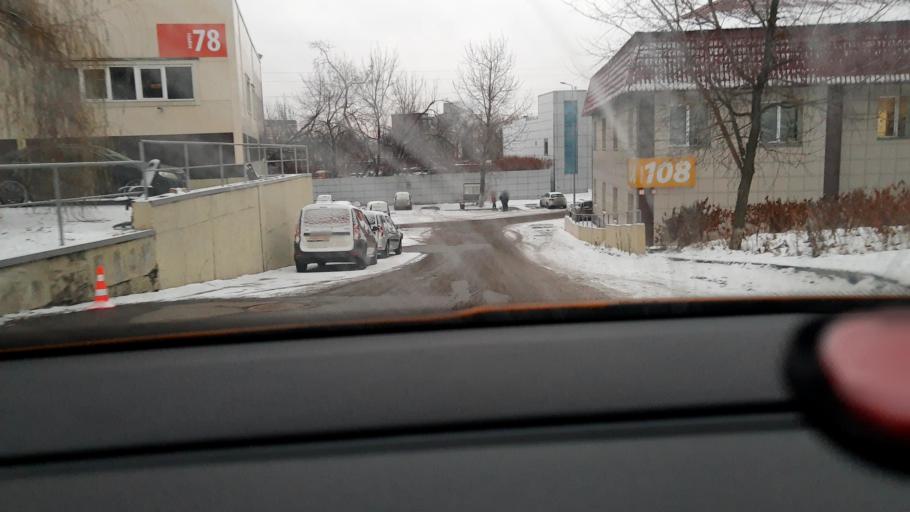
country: RU
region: Moskovskaya
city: Kozhukhovo
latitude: 55.7102
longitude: 37.6907
